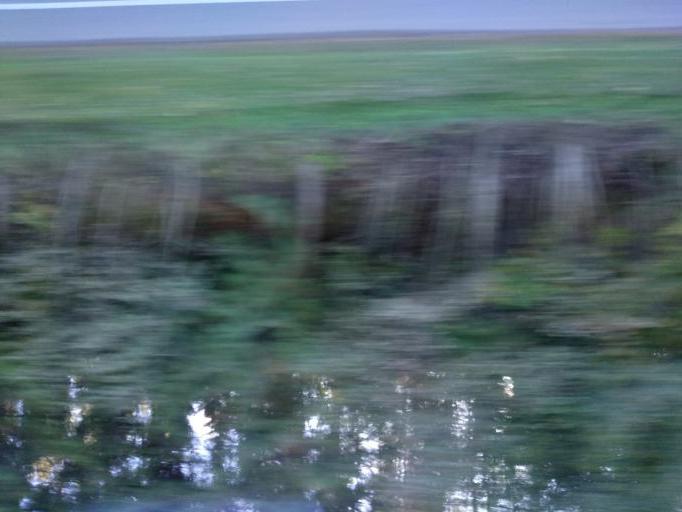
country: EE
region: Polvamaa
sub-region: Polva linn
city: Polva
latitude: 58.0460
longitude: 27.0656
